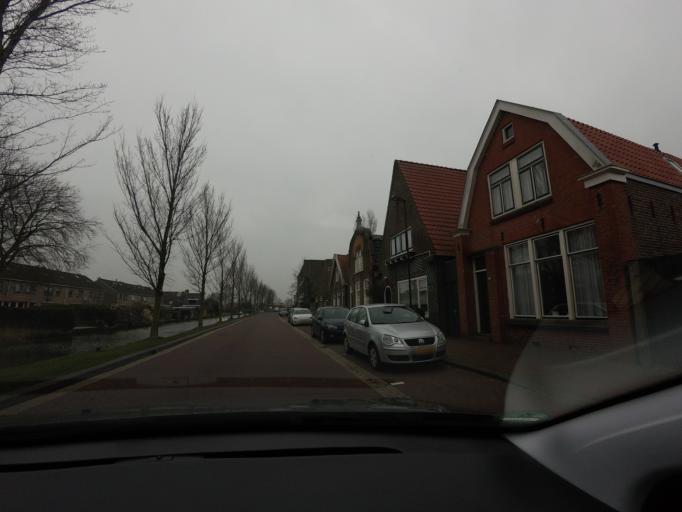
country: NL
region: Friesland
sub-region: Sudwest Fryslan
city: Bolsward
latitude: 53.0646
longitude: 5.5234
